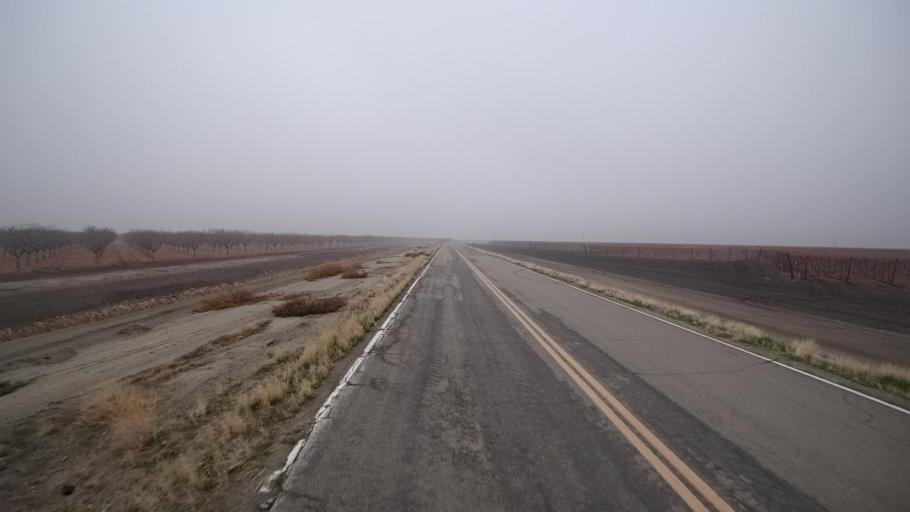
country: US
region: California
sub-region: Kern County
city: Buttonwillow
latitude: 35.4236
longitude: -119.5300
